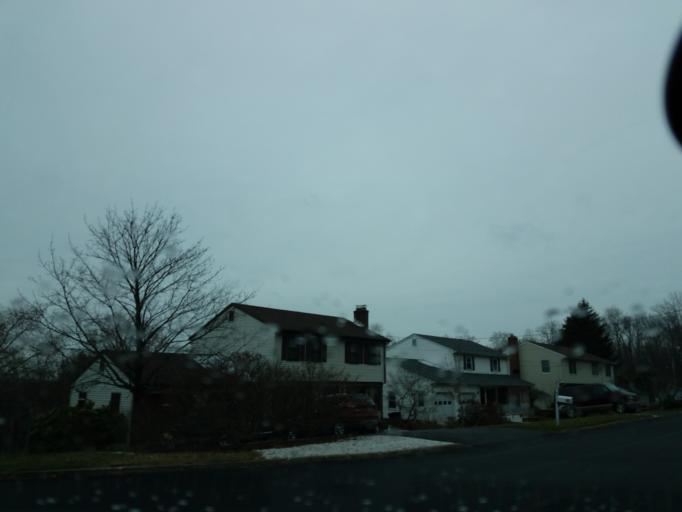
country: US
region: Connecticut
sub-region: Hartford County
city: New Britain
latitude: 41.6978
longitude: -72.7772
